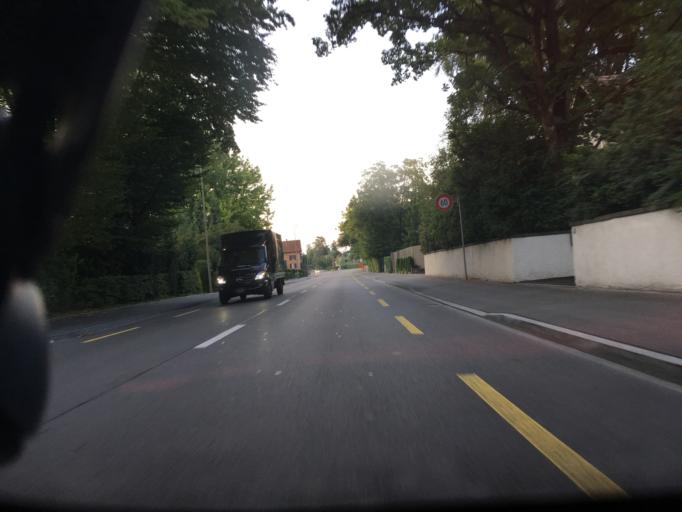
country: CH
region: Zurich
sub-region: Bezirk Meilen
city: Kuesnacht / Dorf
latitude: 47.3123
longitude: 8.5826
